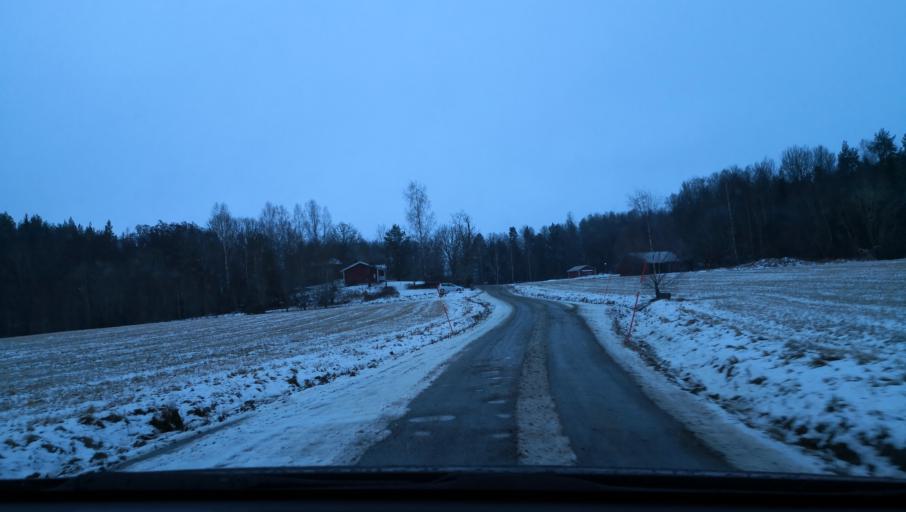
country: SE
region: Vaestmanland
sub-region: Kungsors Kommun
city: Kungsoer
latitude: 59.3983
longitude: 16.2058
